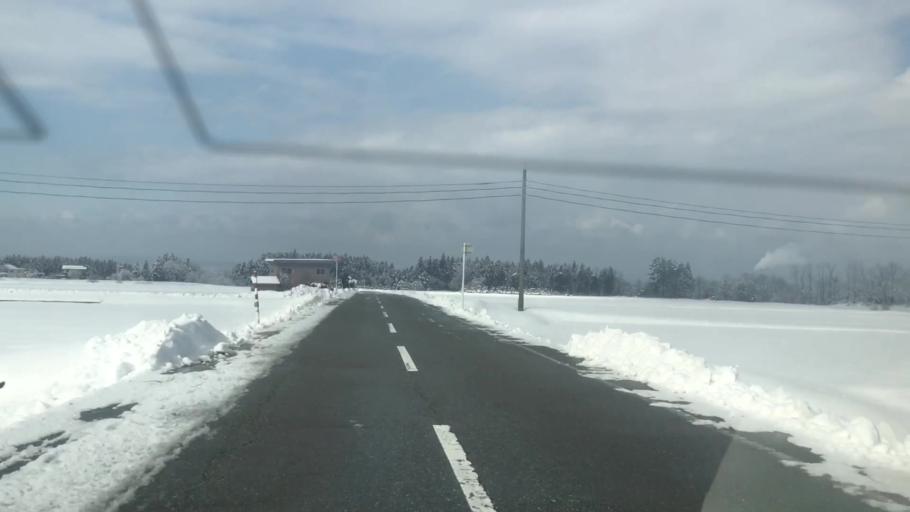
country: JP
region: Toyama
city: Kamiichi
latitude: 36.6005
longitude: 137.3110
